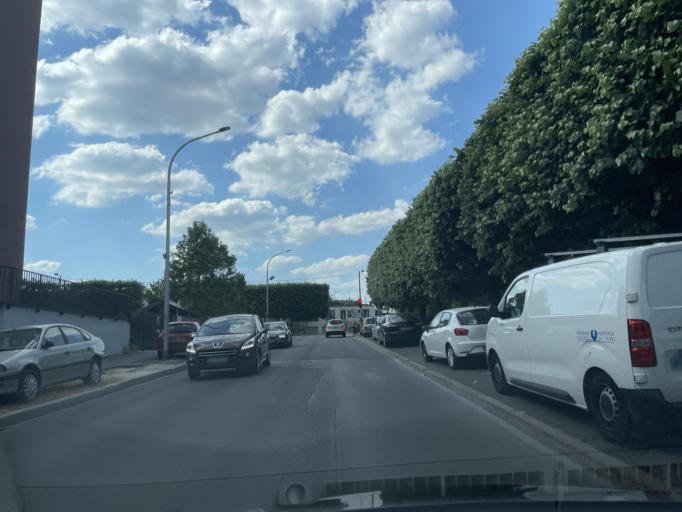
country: FR
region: Ile-de-France
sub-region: Departement du Val-de-Marne
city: Bonneuil-sur-Marne
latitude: 48.7715
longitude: 2.4793
